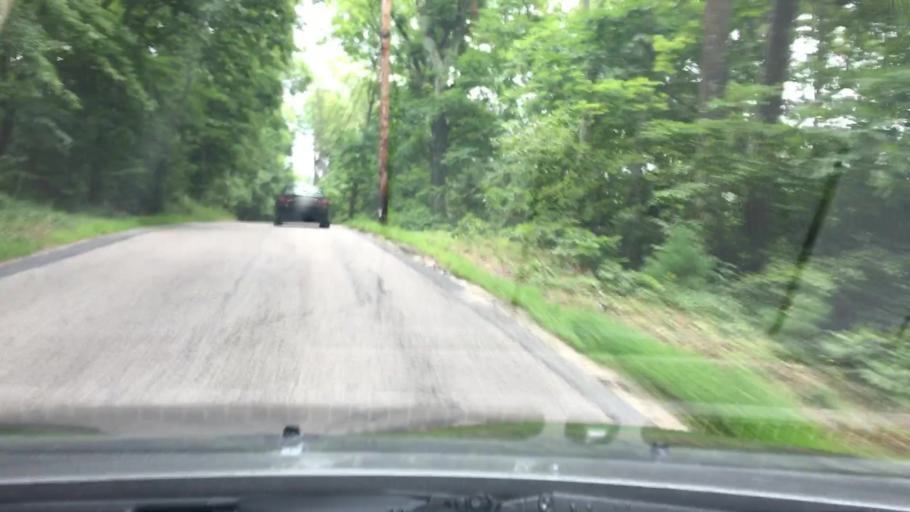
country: US
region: Rhode Island
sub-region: Providence County
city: Cumberland Hill
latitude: 42.0143
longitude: -71.4472
